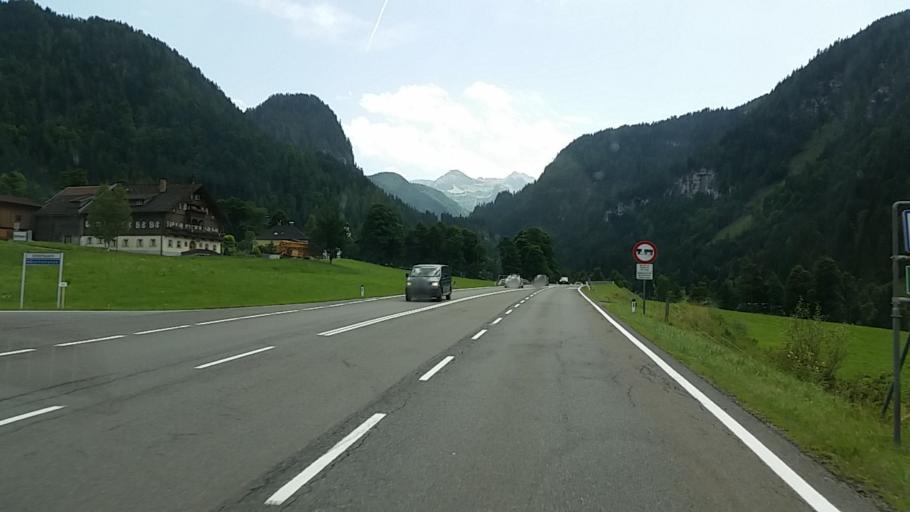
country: AT
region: Salzburg
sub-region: Politischer Bezirk Sankt Johann im Pongau
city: Untertauern
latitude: 47.3076
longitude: 13.5067
